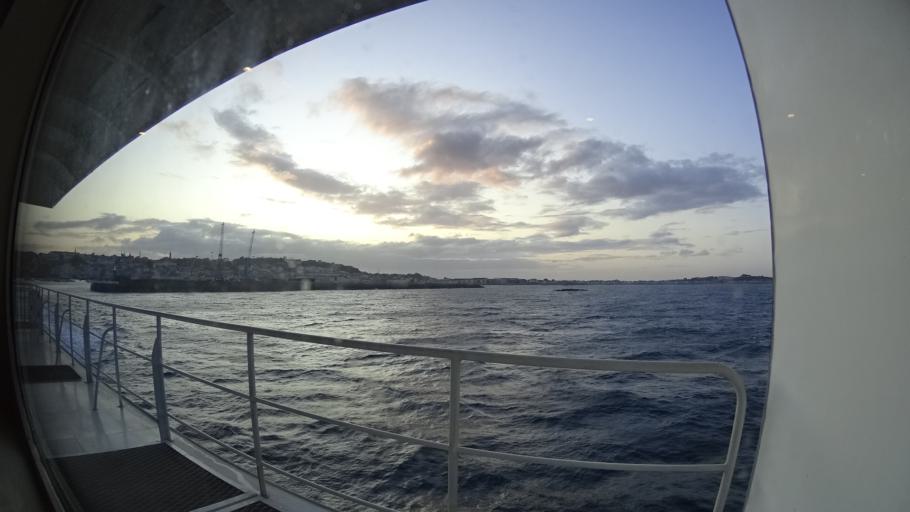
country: GG
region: St Peter Port
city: Saint Peter Port
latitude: 49.4559
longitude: -2.5227
